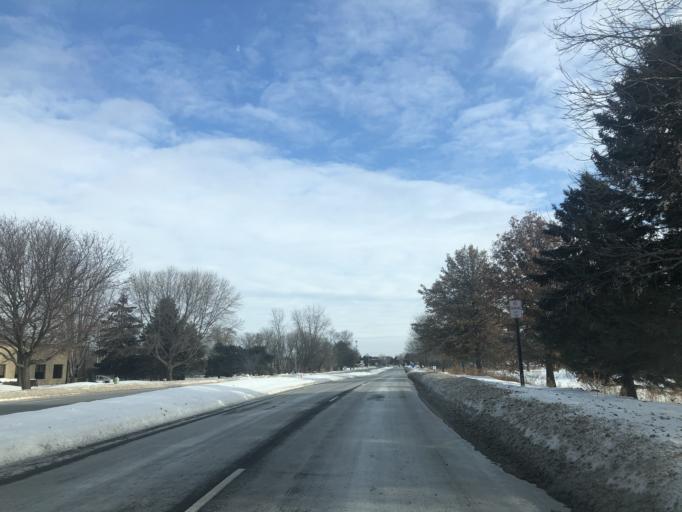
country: US
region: Minnesota
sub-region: Anoka County
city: Lexington
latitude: 45.1623
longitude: -93.1688
